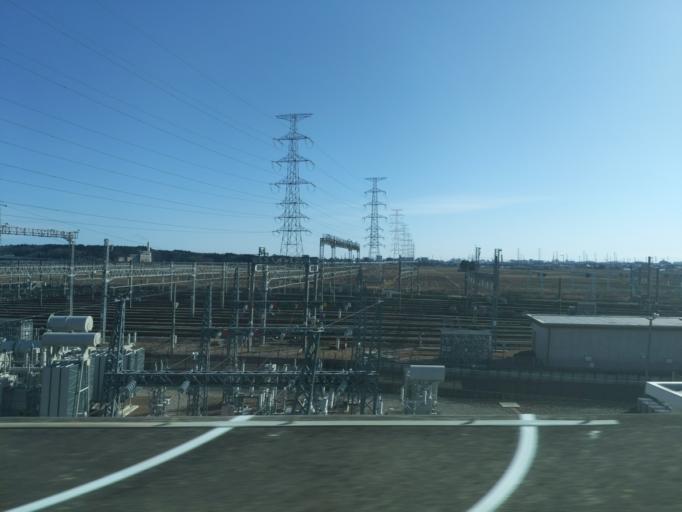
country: JP
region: Miyagi
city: Rifu
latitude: 38.3108
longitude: 140.9641
